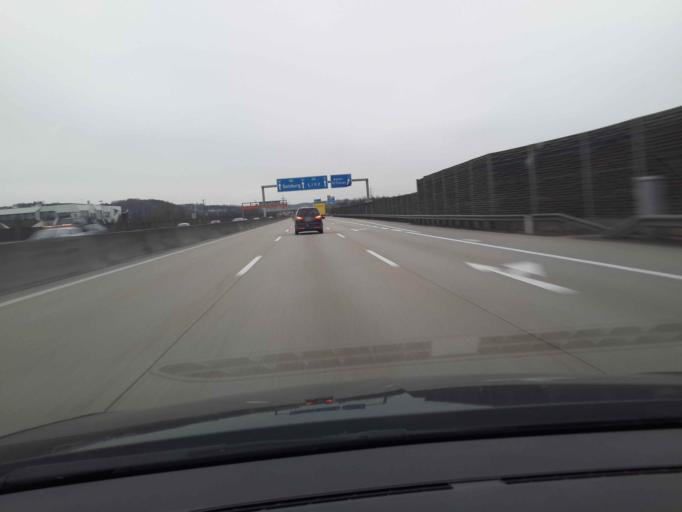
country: AT
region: Upper Austria
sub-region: Politischer Bezirk Linz-Land
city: Asten
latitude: 48.2159
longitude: 14.4140
